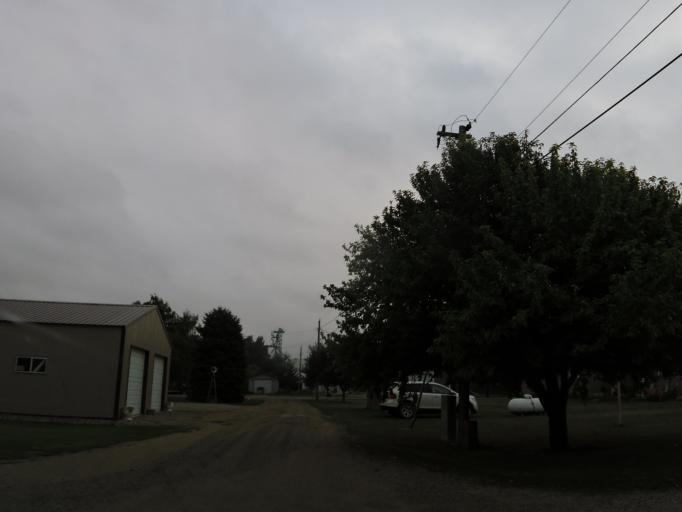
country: US
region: North Dakota
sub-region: Walsh County
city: Grafton
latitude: 48.5575
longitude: -97.1797
